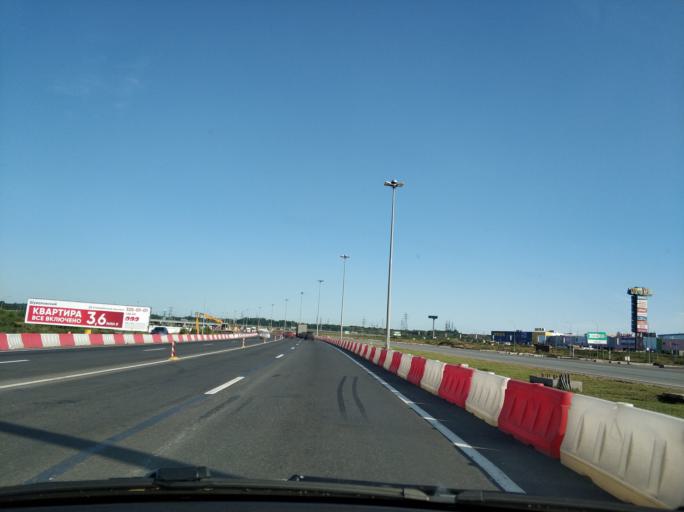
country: RU
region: Leningrad
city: Bugry
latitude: 60.0857
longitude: 30.3771
